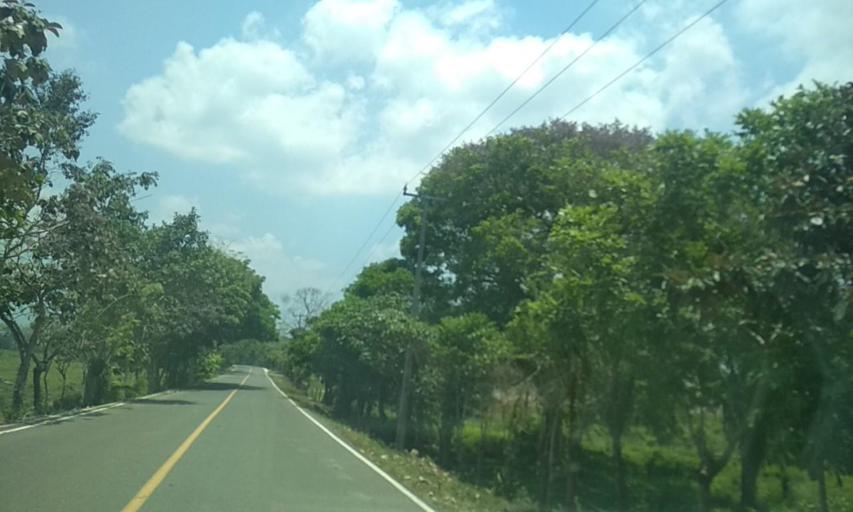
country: MX
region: Tabasco
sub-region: Huimanguillo
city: Francisco Rueda
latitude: 17.7500
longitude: -94.0336
